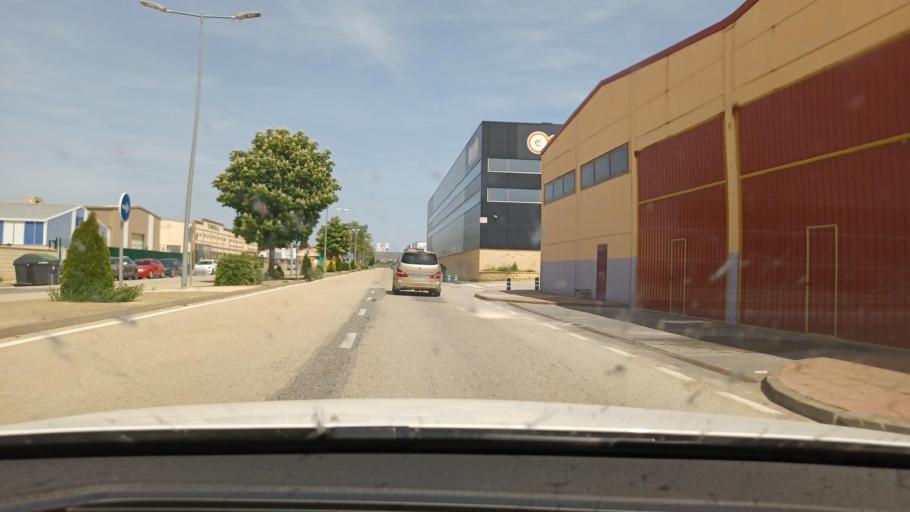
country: ES
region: Castille and Leon
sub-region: Provincia de Soria
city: Almazan
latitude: 41.4701
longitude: -2.5309
